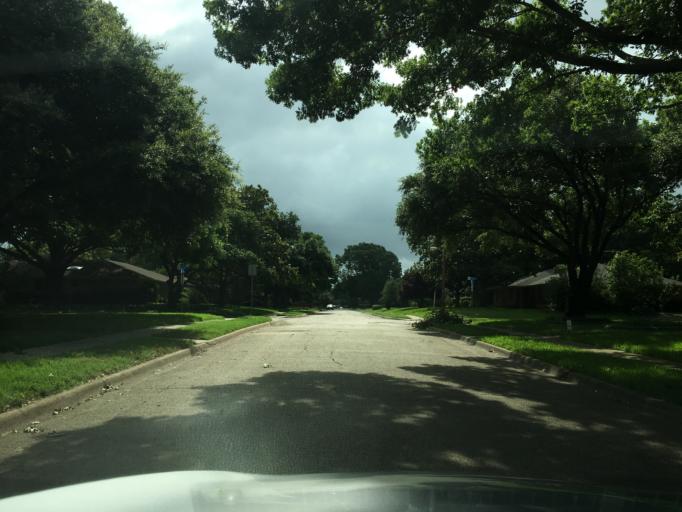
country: US
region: Texas
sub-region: Dallas County
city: Richardson
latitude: 32.9408
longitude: -96.7216
